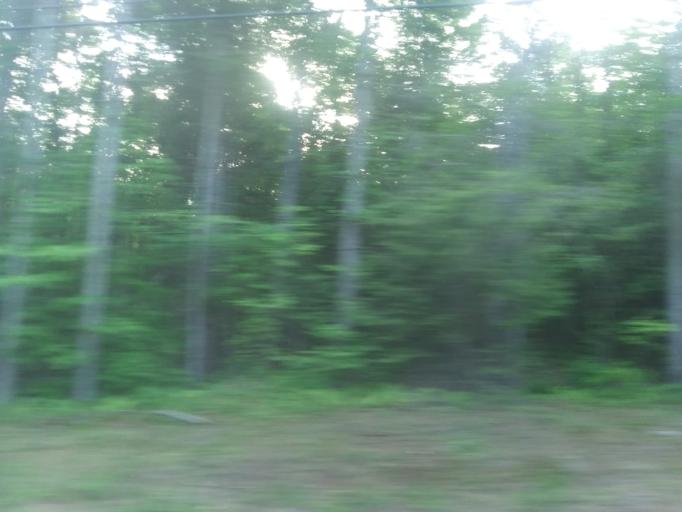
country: US
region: Massachusetts
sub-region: Franklin County
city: Shelburne Falls
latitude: 42.6064
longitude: -72.7611
